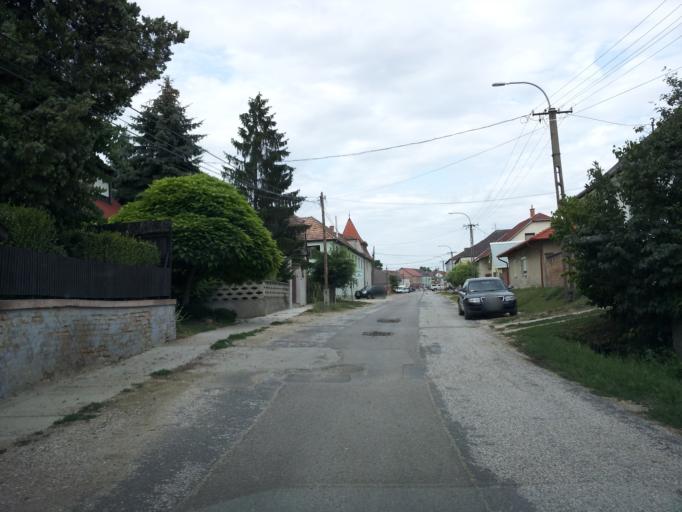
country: HU
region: Fejer
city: Enying
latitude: 46.9286
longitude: 18.2405
